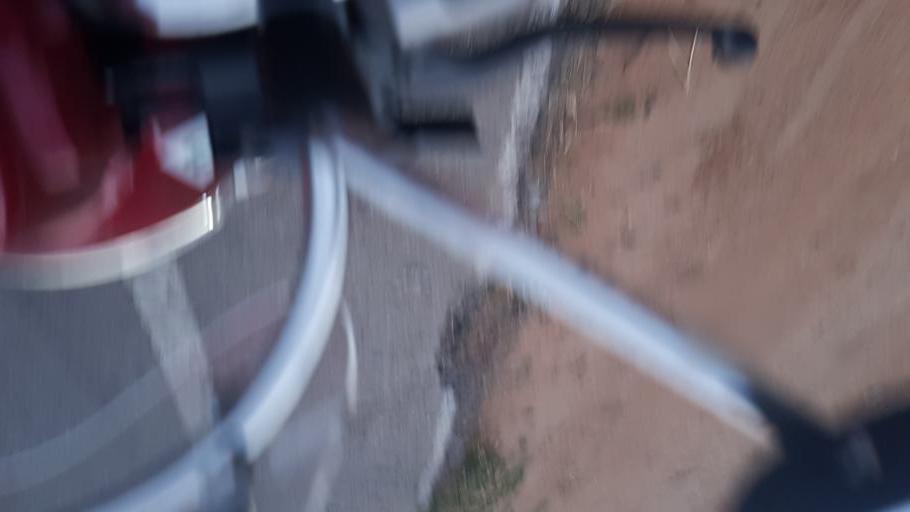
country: TH
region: Nakhon Ratchasima
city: Bua Lai
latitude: 15.6549
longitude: 102.5389
